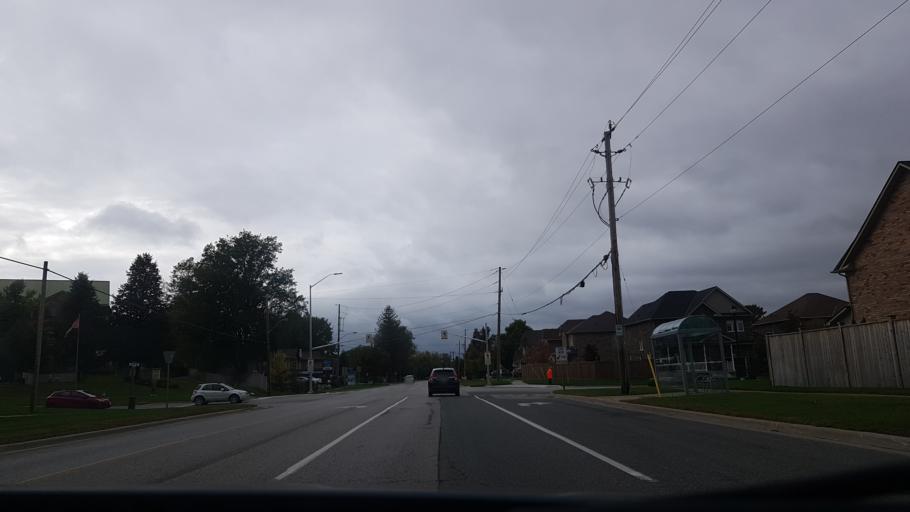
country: CA
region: Ontario
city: Uxbridge
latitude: 44.1043
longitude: -79.1078
